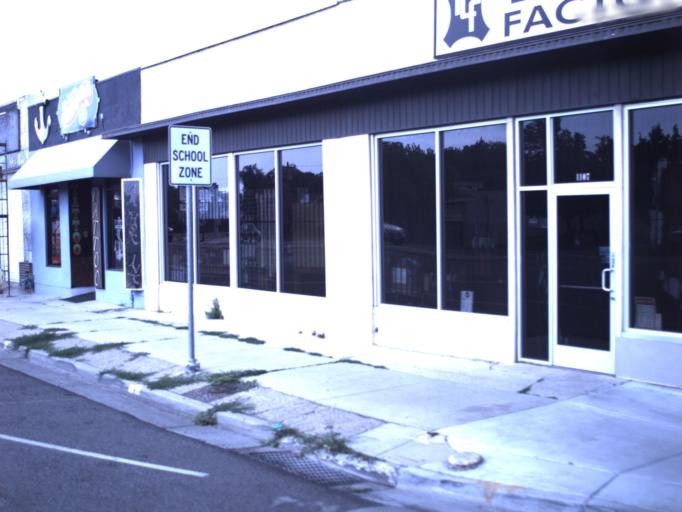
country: US
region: Utah
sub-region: Salt Lake County
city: Salt Lake City
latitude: 40.7449
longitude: -111.8881
